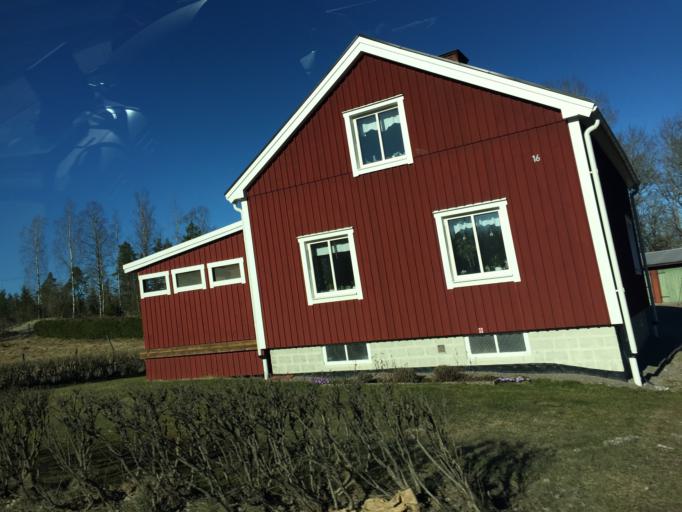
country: SE
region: OEstergoetland
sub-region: Finspangs Kommun
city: Finspang
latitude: 58.7197
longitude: 15.6856
